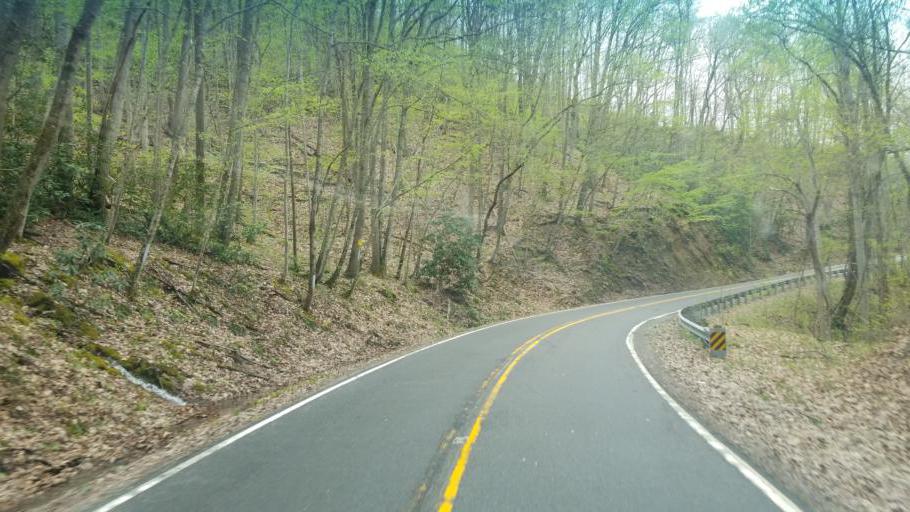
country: US
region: Virginia
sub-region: Tazewell County
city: Tazewell
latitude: 37.0039
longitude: -81.5194
